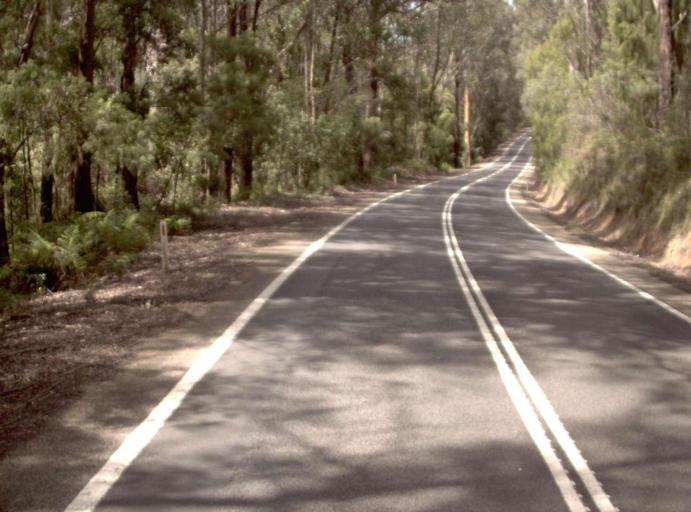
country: AU
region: New South Wales
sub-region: Bombala
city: Bombala
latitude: -37.5369
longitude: 149.3691
